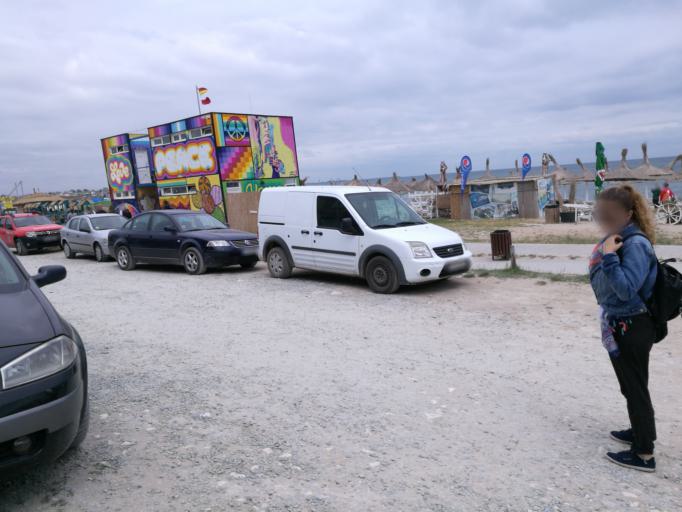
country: RO
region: Constanta
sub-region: Municipiul Mangalia
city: Mangalia
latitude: 43.7514
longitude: 28.5759
